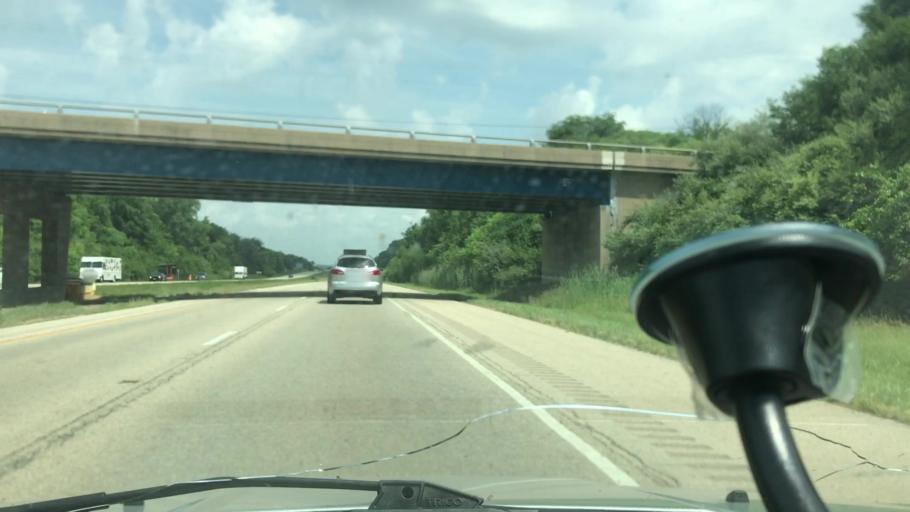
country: US
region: Illinois
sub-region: Peoria County
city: Bellevue
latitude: 40.6980
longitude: -89.6756
